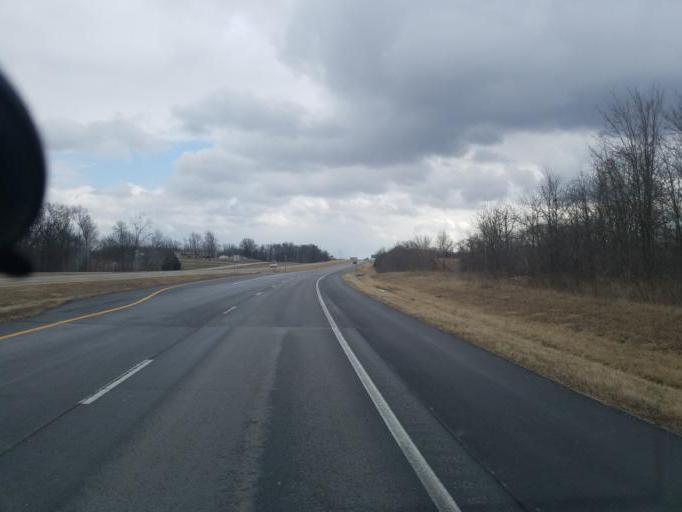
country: US
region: Missouri
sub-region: Randolph County
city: Moberly
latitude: 39.2647
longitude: -92.3367
